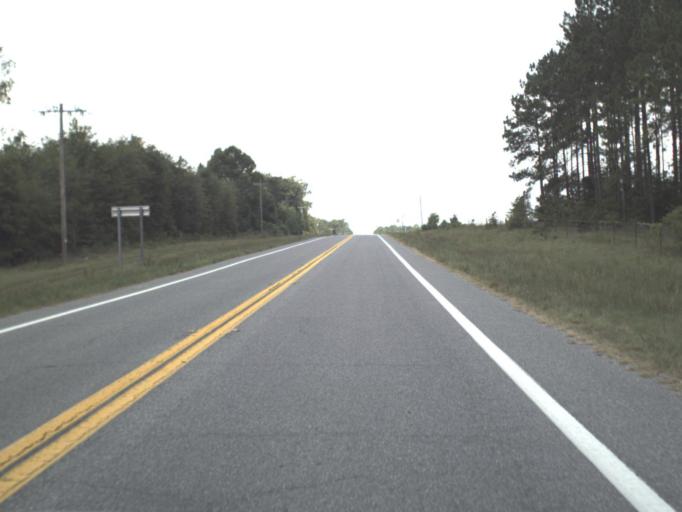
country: US
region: Florida
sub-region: Hamilton County
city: Jasper
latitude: 30.4901
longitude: -83.1340
